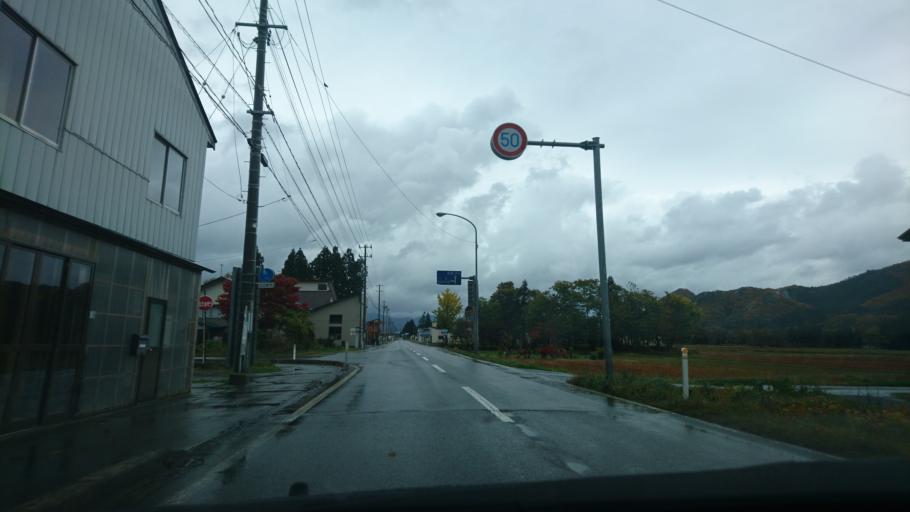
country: JP
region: Akita
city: Yokotemachi
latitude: 39.3675
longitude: 140.7613
